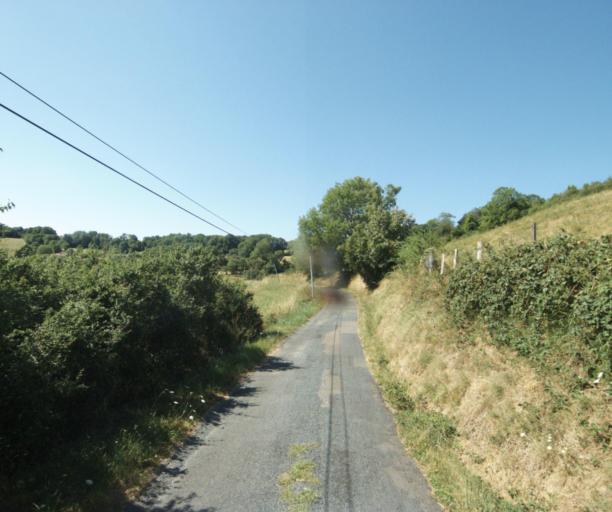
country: FR
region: Rhone-Alpes
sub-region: Departement du Rhone
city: Montrottier
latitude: 45.8127
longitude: 4.4908
